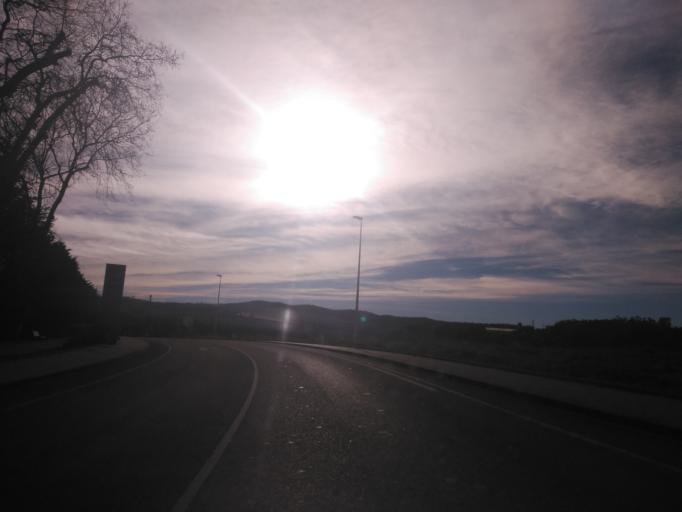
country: ES
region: Cantabria
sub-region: Provincia de Cantabria
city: Comillas
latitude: 43.3786
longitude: -4.2894
